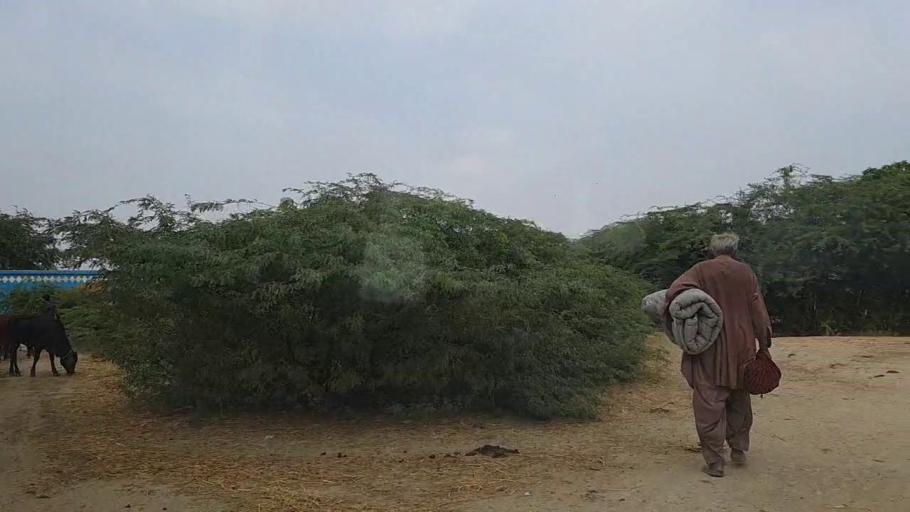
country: PK
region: Sindh
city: Mirpur Sakro
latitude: 24.6032
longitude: 67.6987
